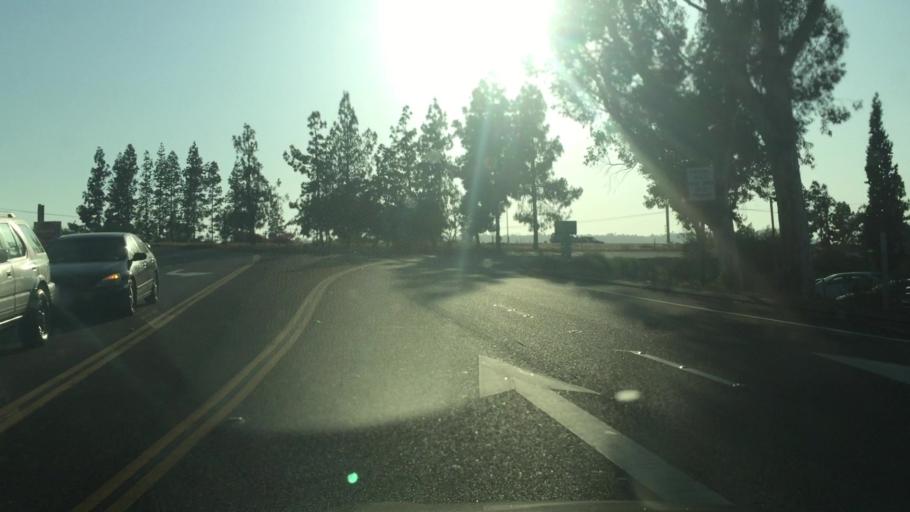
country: US
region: California
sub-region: San Diego County
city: El Cajon
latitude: 32.8086
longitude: -116.9605
